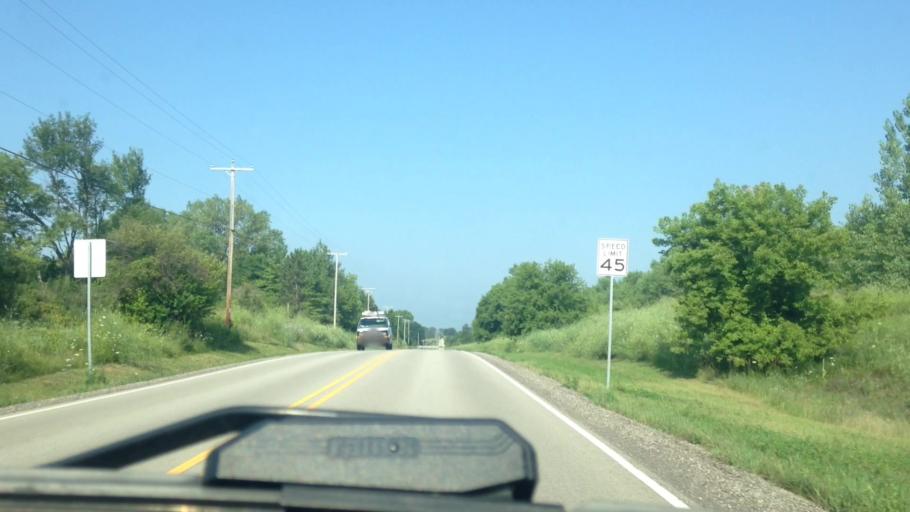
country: US
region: Wisconsin
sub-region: Waukesha County
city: Merton
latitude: 43.1631
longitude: -88.2774
